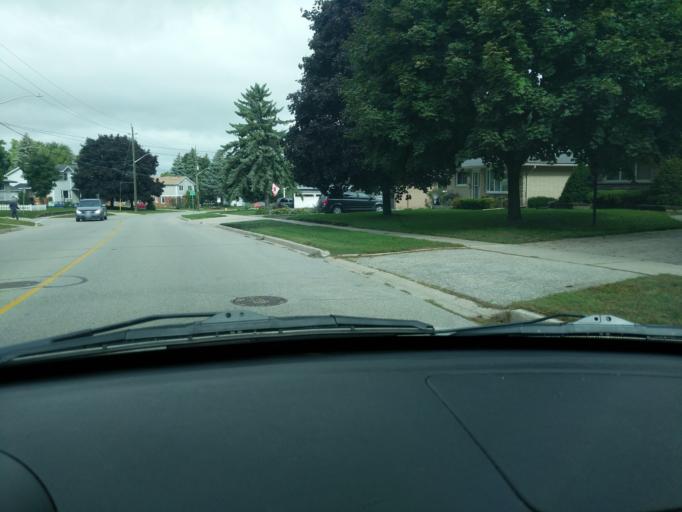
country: CA
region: Ontario
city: Cambridge
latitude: 43.4218
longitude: -80.3145
